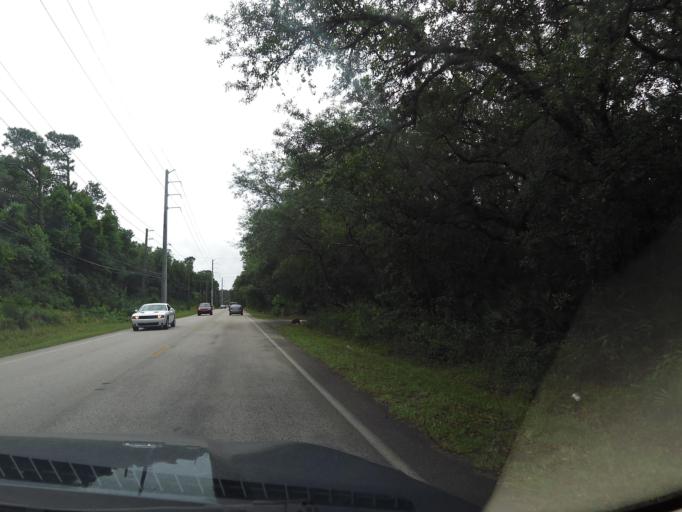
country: US
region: Florida
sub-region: Saint Johns County
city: Saint Augustine
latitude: 29.9123
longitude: -81.3670
